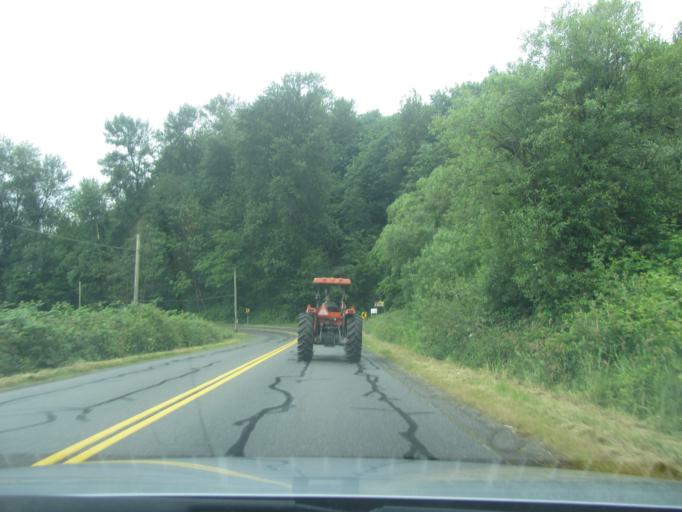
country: CA
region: British Columbia
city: Abbotsford
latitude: 49.1039
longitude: -122.3509
